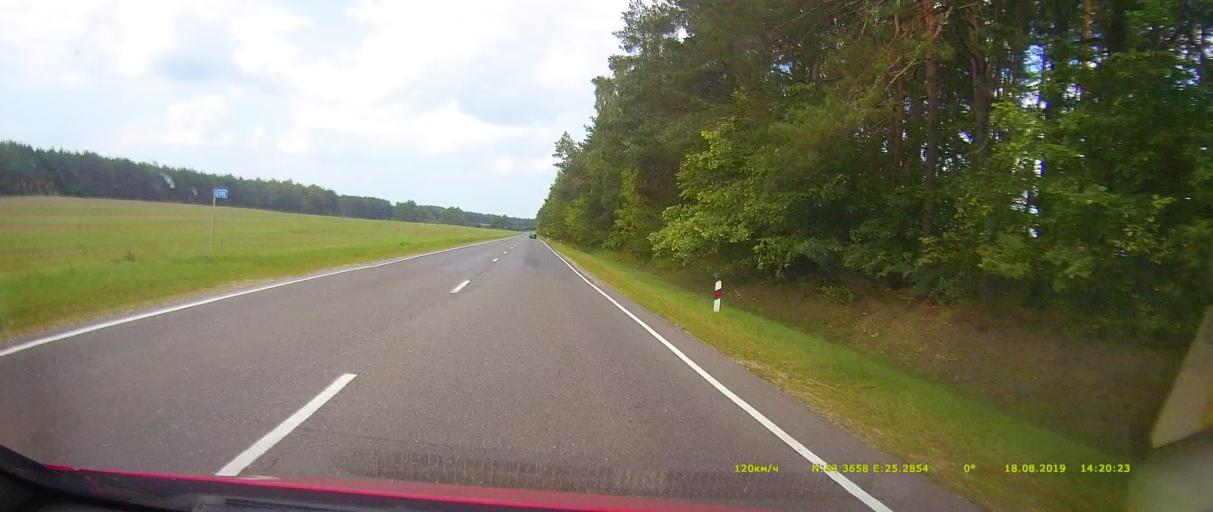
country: BY
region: Grodnenskaya
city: Dzyatlava
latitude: 53.3831
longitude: 25.2926
